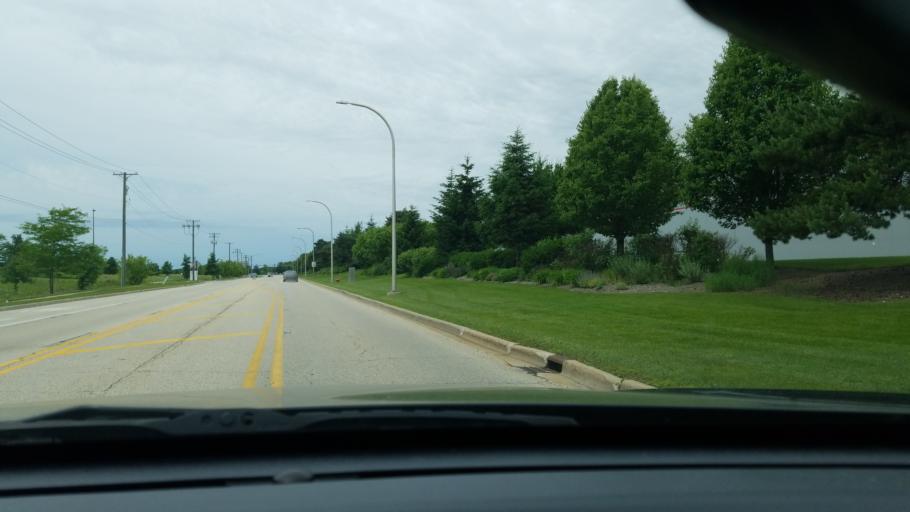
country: US
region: Illinois
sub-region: Kane County
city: Sleepy Hollow
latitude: 42.0731
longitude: -88.3293
